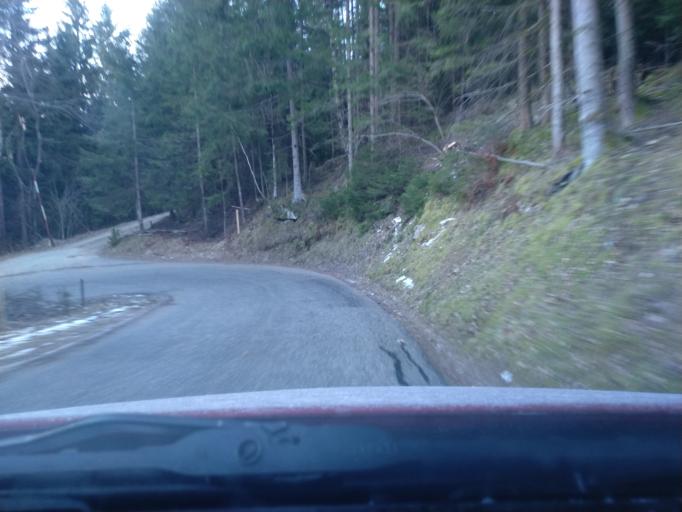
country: AT
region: Carinthia
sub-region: Politischer Bezirk Villach Land
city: Arriach
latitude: 46.7230
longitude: 13.8830
